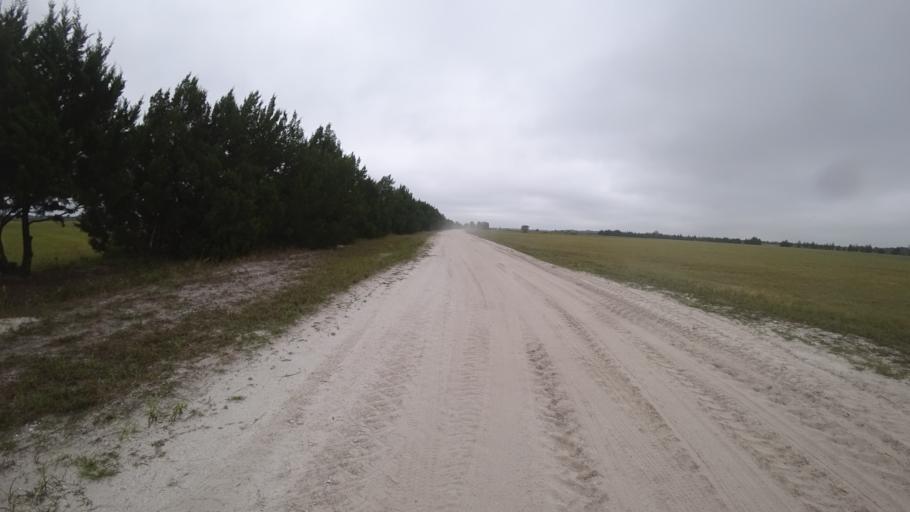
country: US
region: Florida
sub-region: Sarasota County
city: Warm Mineral Springs
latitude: 27.2996
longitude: -82.1346
